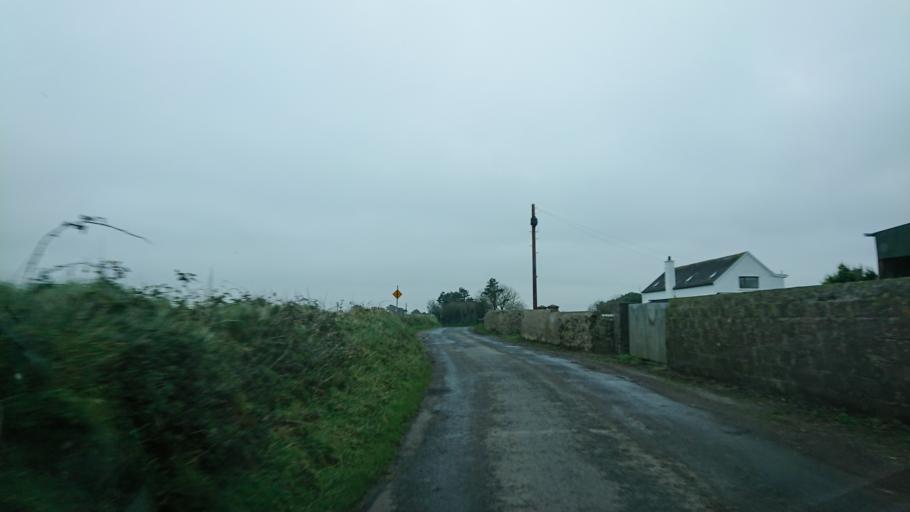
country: IE
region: Munster
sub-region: Waterford
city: Dunmore East
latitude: 52.1608
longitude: -7.0360
